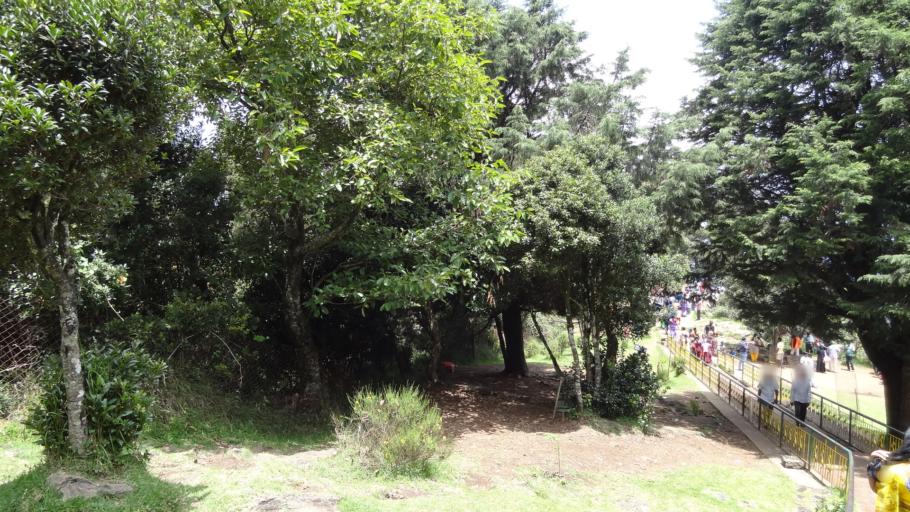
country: IN
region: Tamil Nadu
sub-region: Nilgiri
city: Aravankadu
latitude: 11.4005
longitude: 76.7354
